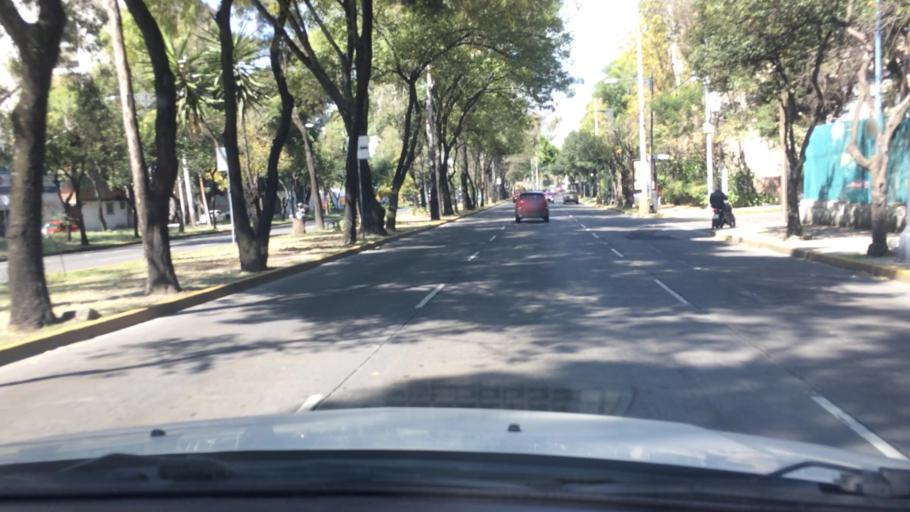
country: MX
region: Mexico City
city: Coyoacan
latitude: 19.3318
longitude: -99.1446
